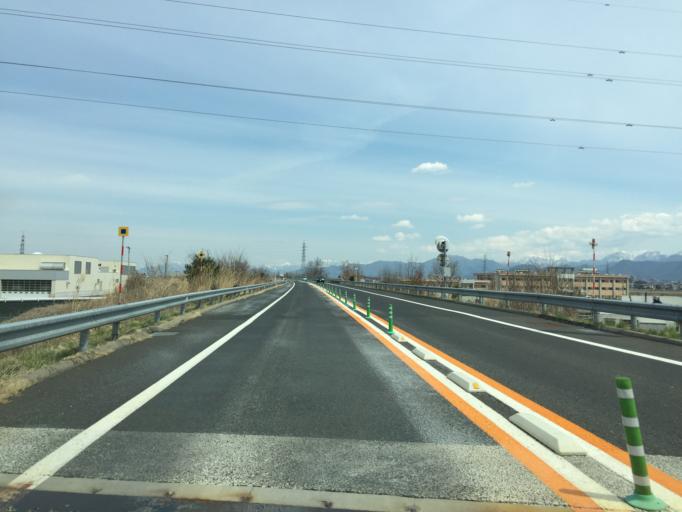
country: JP
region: Yamagata
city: Yamagata-shi
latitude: 38.2503
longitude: 140.2834
